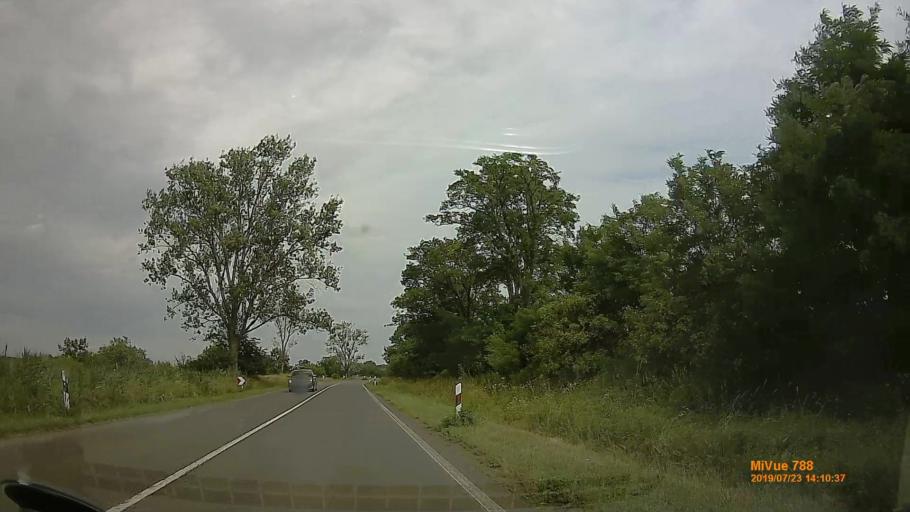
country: HU
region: Szabolcs-Szatmar-Bereg
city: Tiszalok
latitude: 47.9587
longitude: 21.4198
